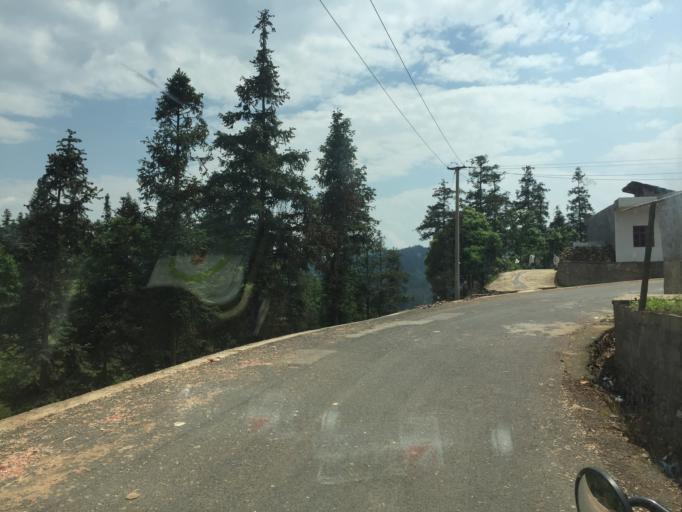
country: CN
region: Guangxi Zhuangzu Zizhiqu
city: Xinzhou
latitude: 25.6946
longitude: 105.2295
